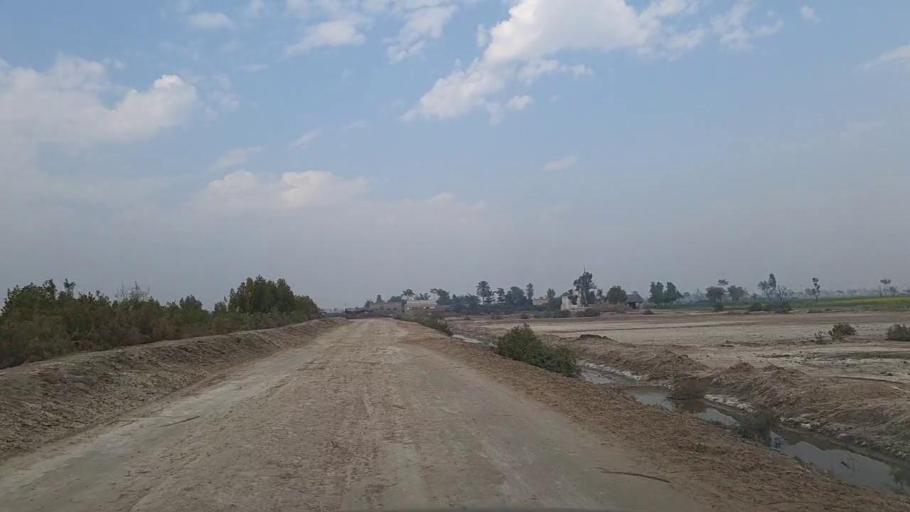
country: PK
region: Sindh
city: Daur
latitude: 26.3708
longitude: 68.3898
